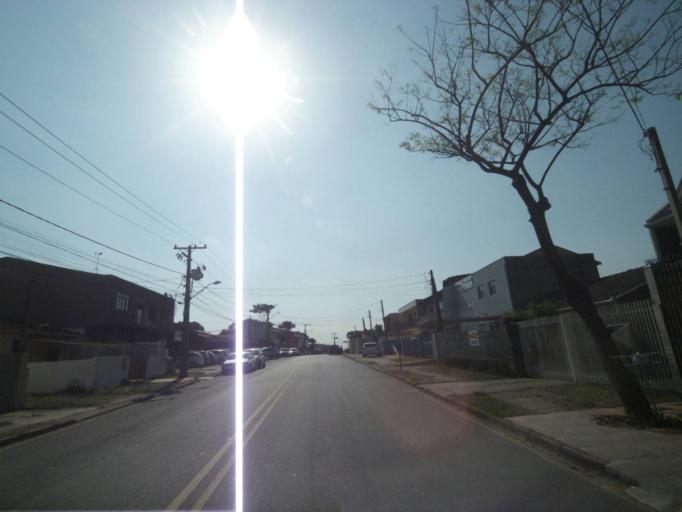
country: BR
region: Parana
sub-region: Curitiba
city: Curitiba
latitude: -25.4830
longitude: -49.3237
